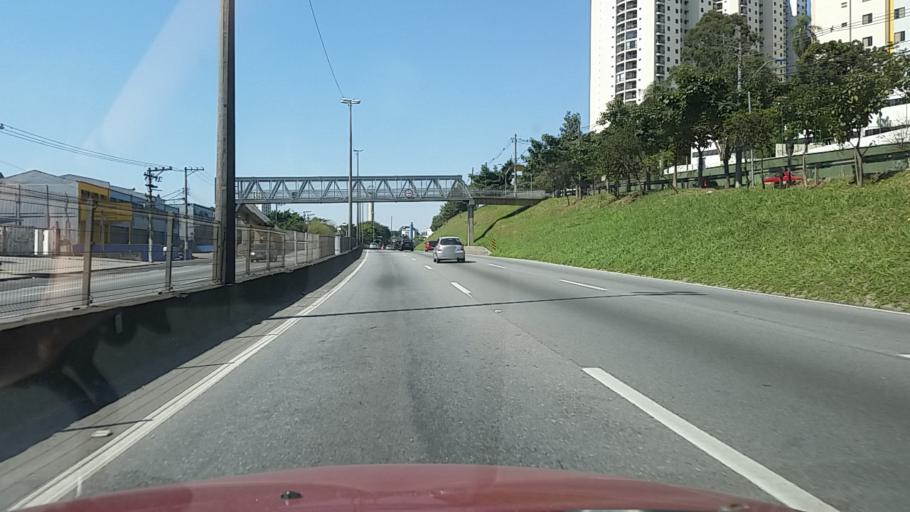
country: BR
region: Sao Paulo
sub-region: Taboao Da Serra
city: Taboao da Serra
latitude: -23.6090
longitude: -46.7697
